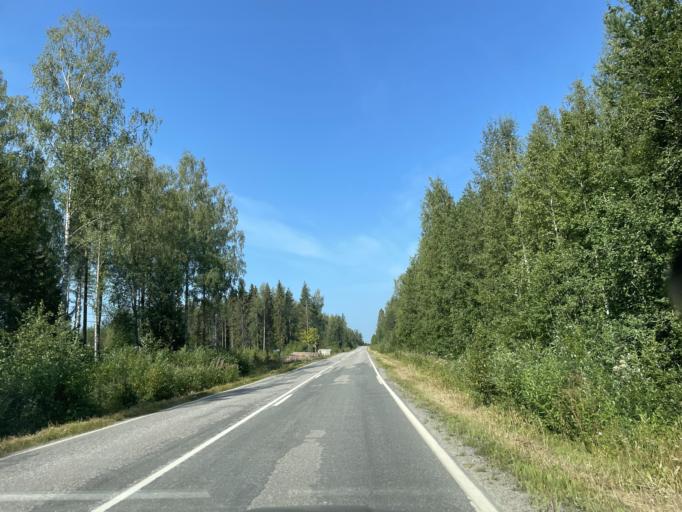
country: FI
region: Central Finland
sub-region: Saarijaervi-Viitasaari
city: Pihtipudas
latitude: 63.3675
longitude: 25.6279
